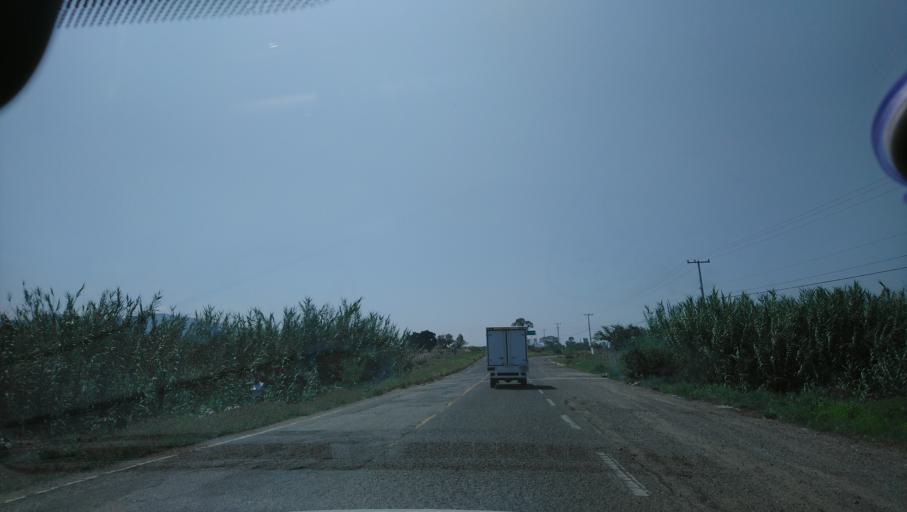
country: MX
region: Oaxaca
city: Santa Maria del Tule
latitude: 17.0395
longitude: -96.6215
